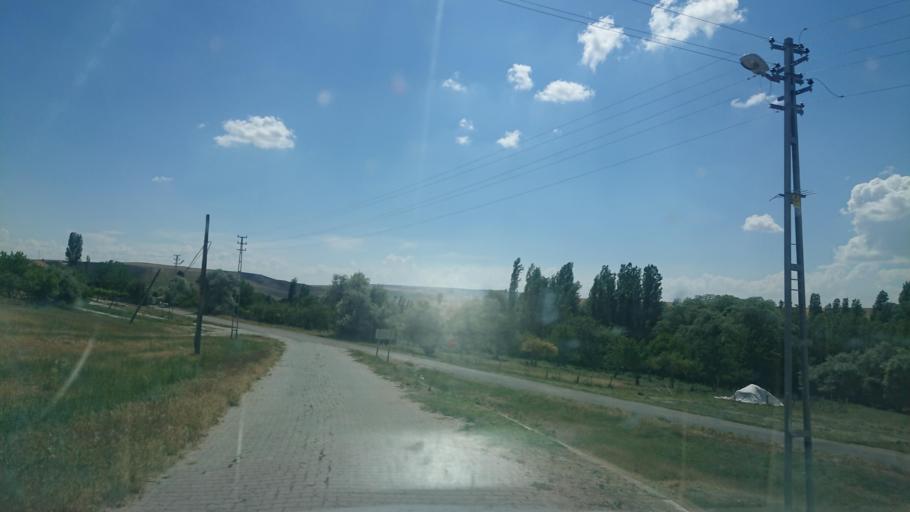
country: TR
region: Aksaray
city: Agacoren
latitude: 38.8294
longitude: 33.7945
